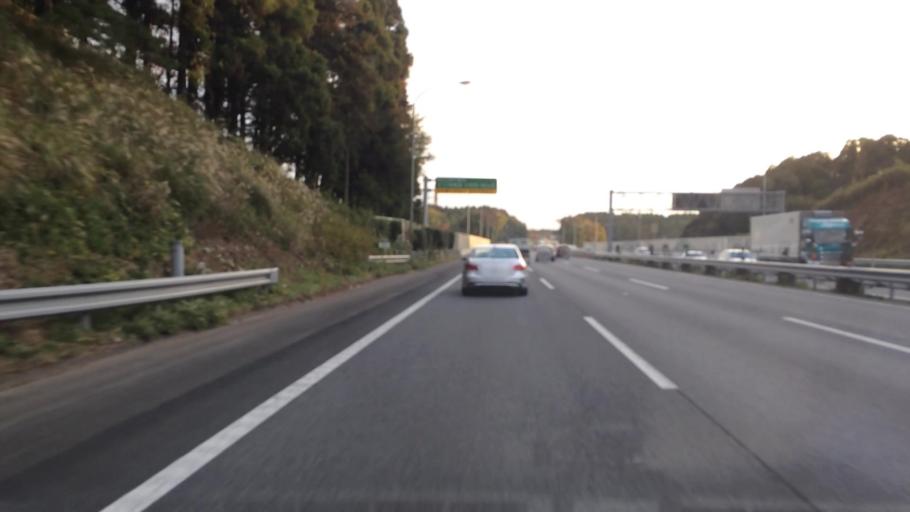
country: JP
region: Chiba
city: Shisui
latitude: 35.7209
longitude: 140.2903
